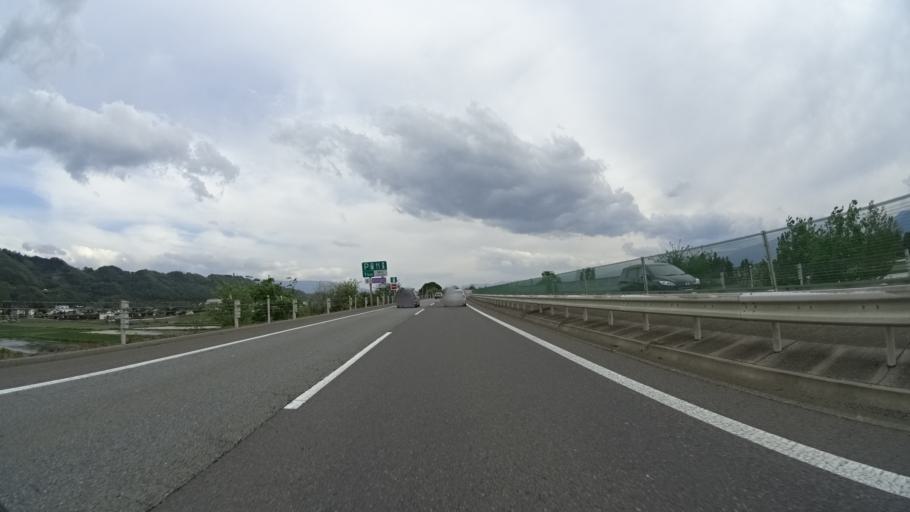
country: JP
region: Nagano
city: Toyoshina
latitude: 36.2823
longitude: 137.9309
